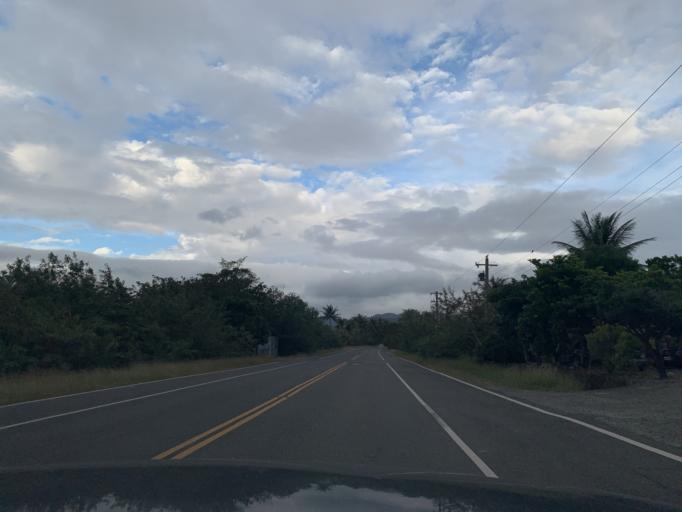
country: TW
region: Taiwan
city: Hengchun
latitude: 22.0511
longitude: 120.7118
